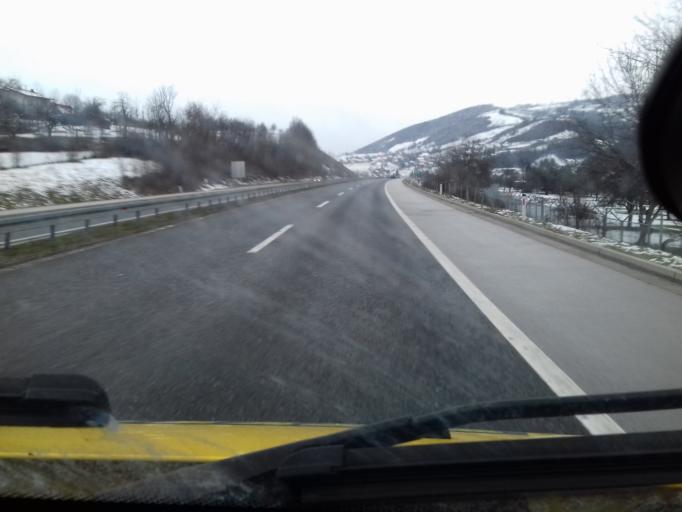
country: BA
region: Federation of Bosnia and Herzegovina
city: Visoko
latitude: 43.9947
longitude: 18.1913
